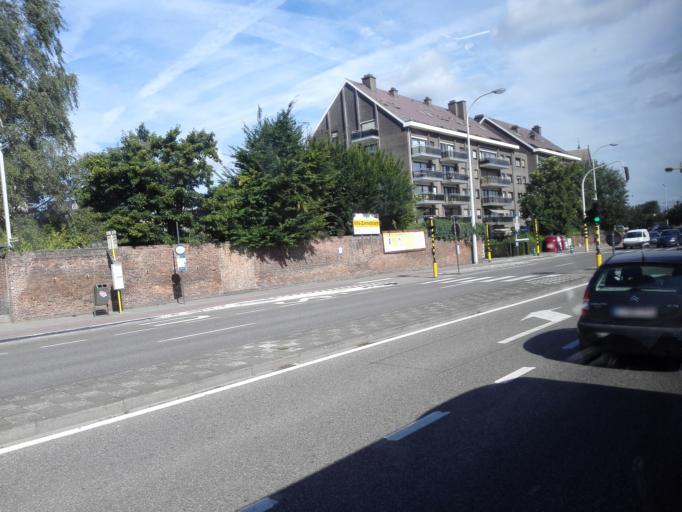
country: BE
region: Flanders
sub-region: Provincie Antwerpen
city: Mechelen
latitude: 51.0263
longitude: 4.4893
